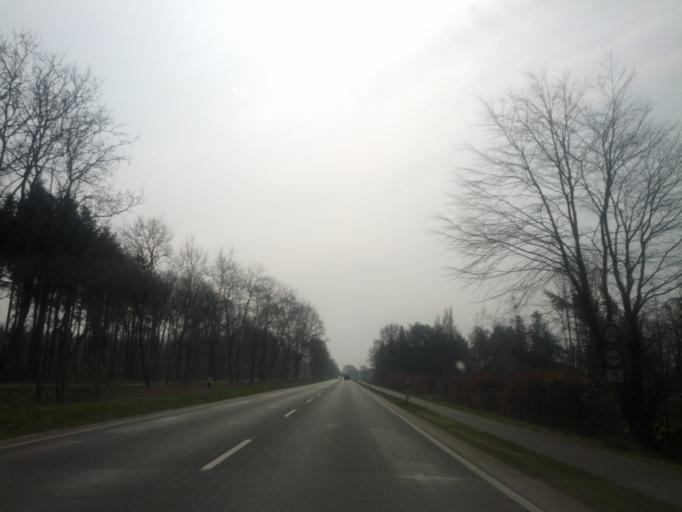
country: DE
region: Lower Saxony
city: Lutetsburg
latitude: 53.5714
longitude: 7.2399
